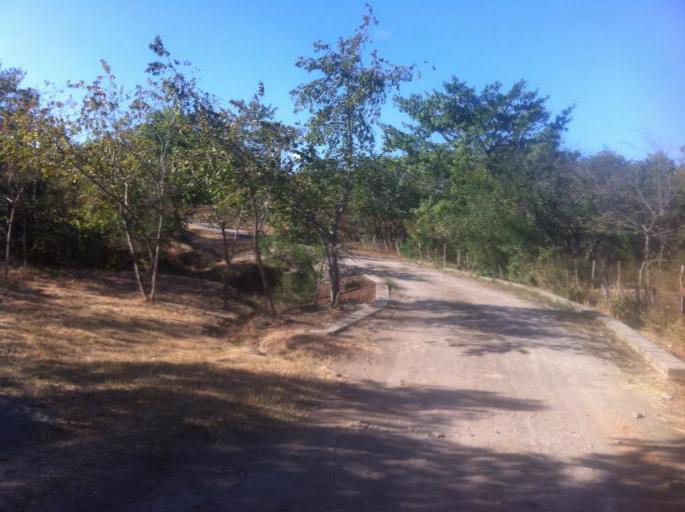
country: NI
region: Managua
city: Carlos Fonseca Amador
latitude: 11.9071
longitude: -86.6059
